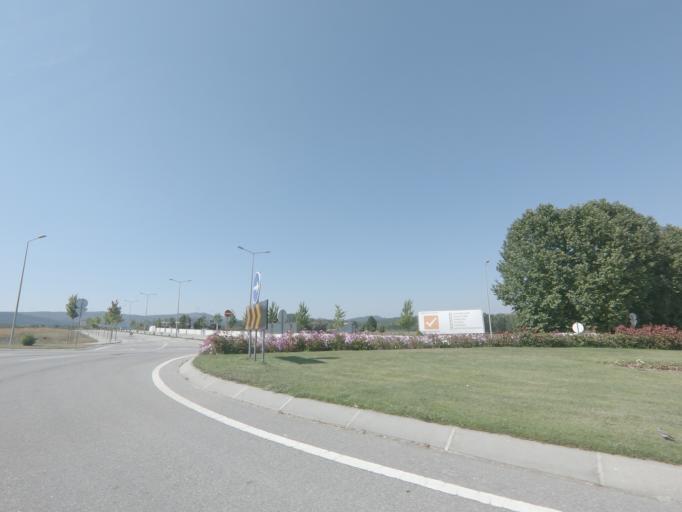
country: PT
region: Viseu
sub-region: Moimenta da Beira
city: Moimenta da Beira
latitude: 40.9841
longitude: -7.6320
